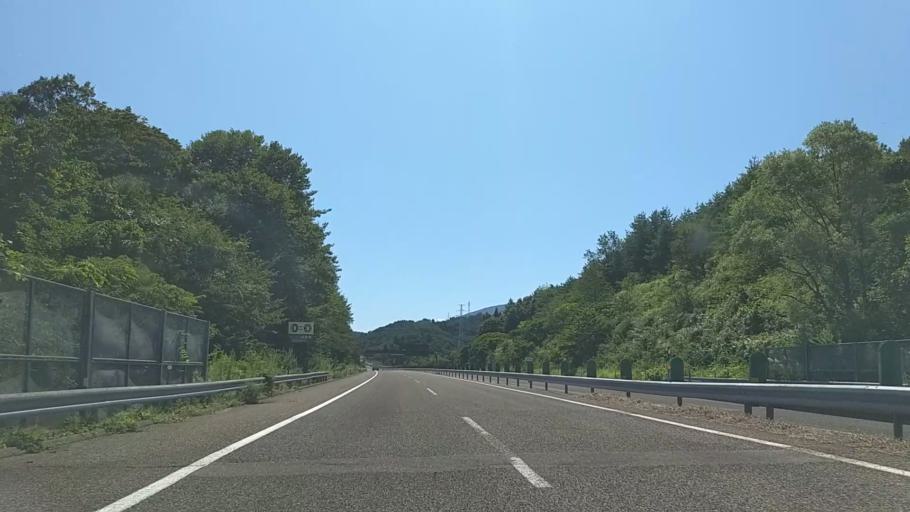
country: JP
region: Niigata
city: Joetsu
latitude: 37.1349
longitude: 138.2134
